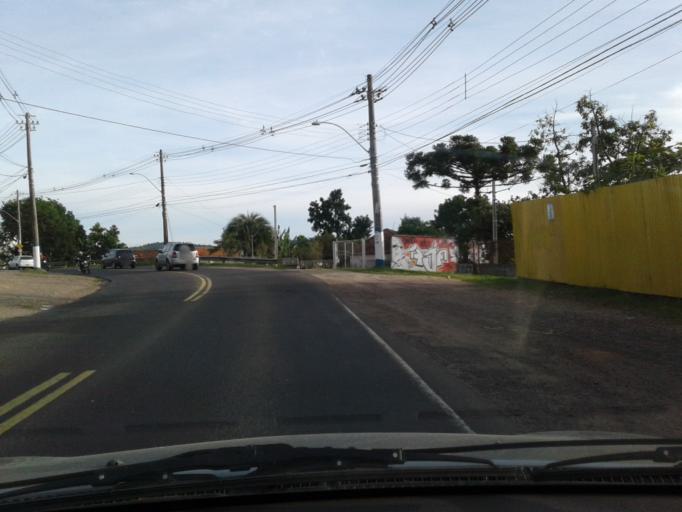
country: BR
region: Rio Grande do Sul
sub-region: Porto Alegre
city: Porto Alegre
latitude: -30.0983
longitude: -51.2252
